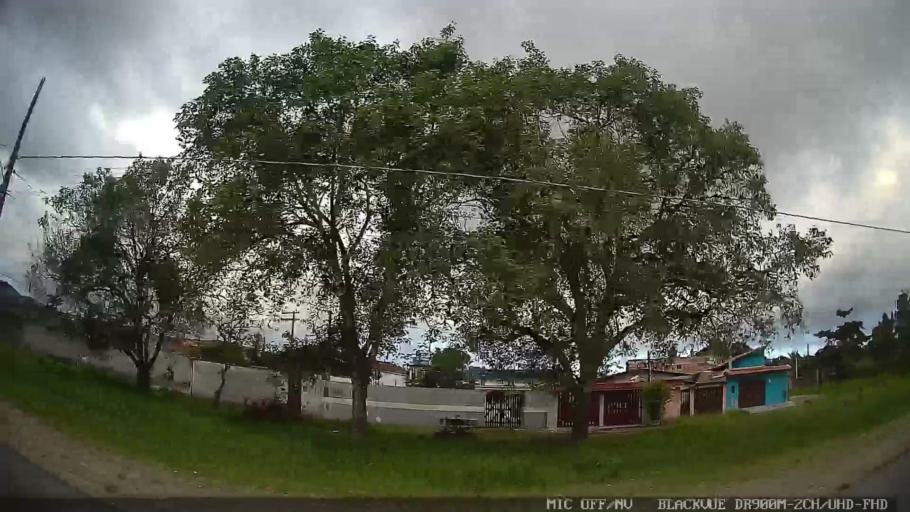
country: BR
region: Sao Paulo
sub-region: Itanhaem
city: Itanhaem
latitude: -24.1545
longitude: -46.7801
